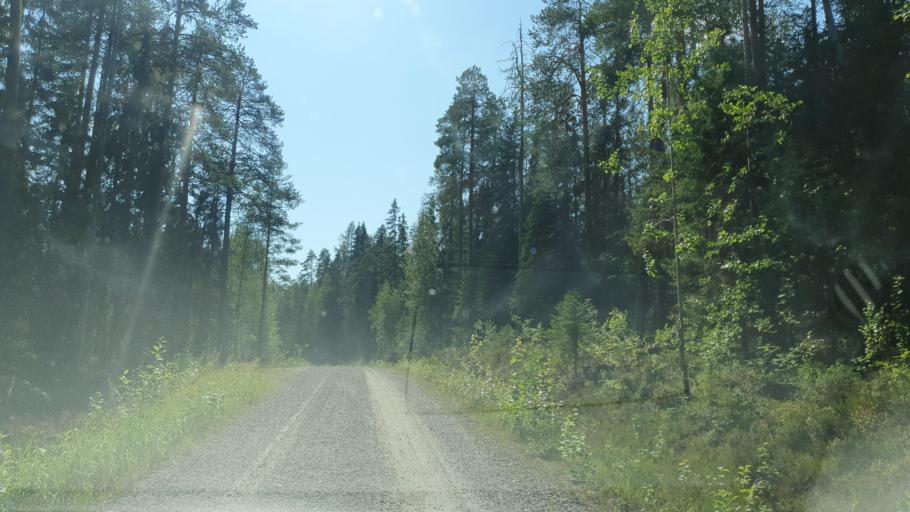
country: FI
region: Kainuu
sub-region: Kehys-Kainuu
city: Kuhmo
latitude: 63.9753
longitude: 29.5391
